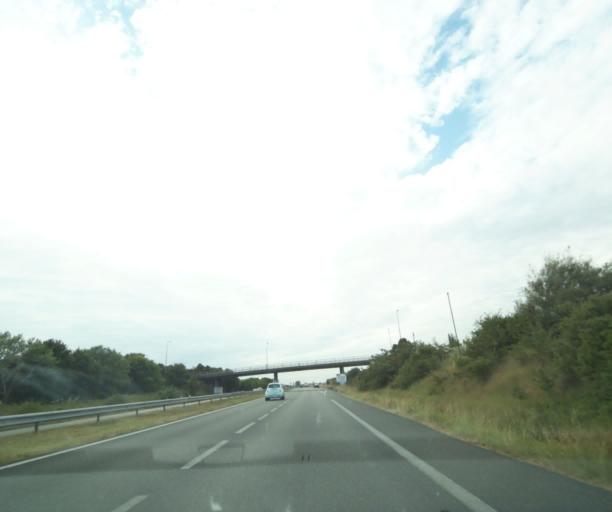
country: FR
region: Poitou-Charentes
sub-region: Departement de la Charente-Maritime
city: Angoulins
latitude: 46.1033
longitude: -1.0948
